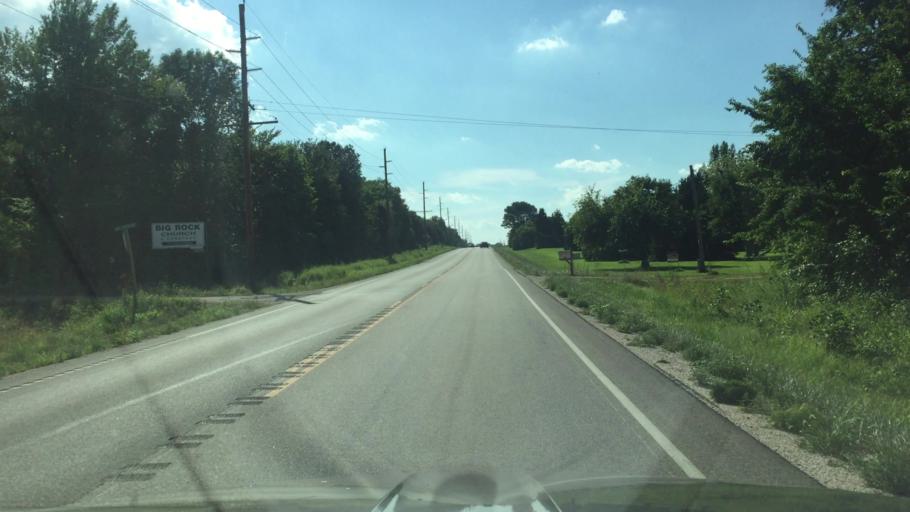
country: US
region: Missouri
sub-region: Morgan County
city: Versailles
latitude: 38.4006
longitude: -92.7415
